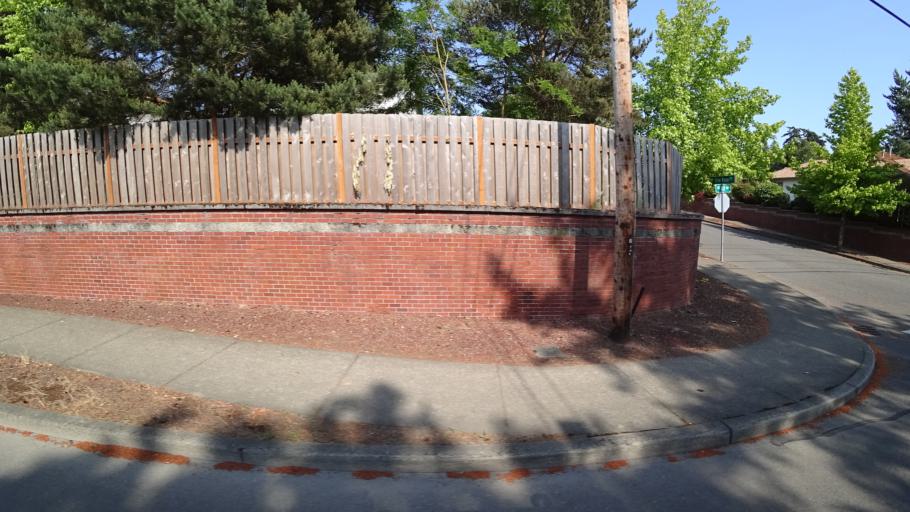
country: US
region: Oregon
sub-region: Clackamas County
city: Sunnyside
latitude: 45.4312
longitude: -122.5381
